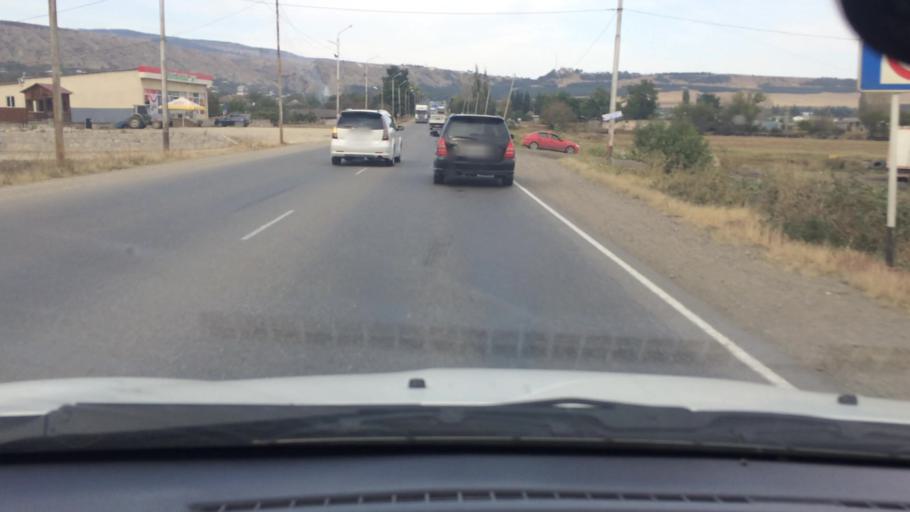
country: GE
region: T'bilisi
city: Tbilisi
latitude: 41.6070
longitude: 44.7833
